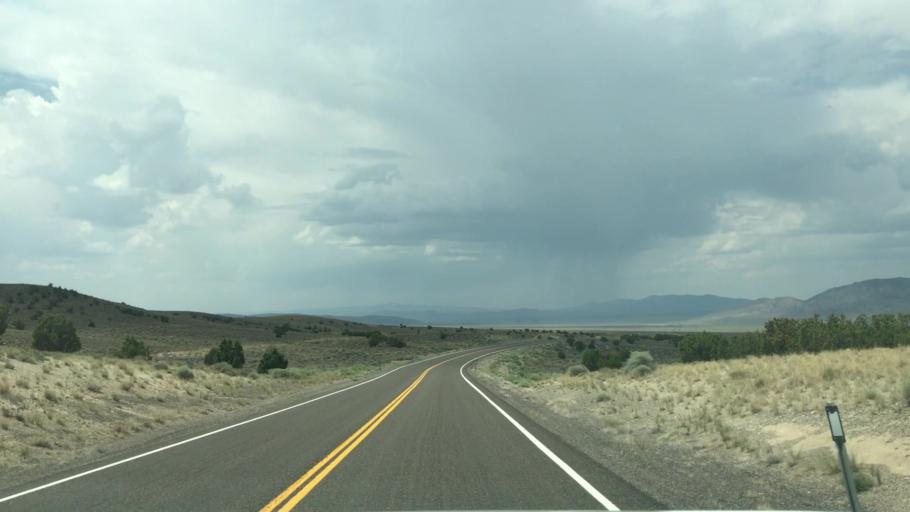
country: US
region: Nevada
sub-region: Eureka County
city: Eureka
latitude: 39.3943
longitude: -115.7221
